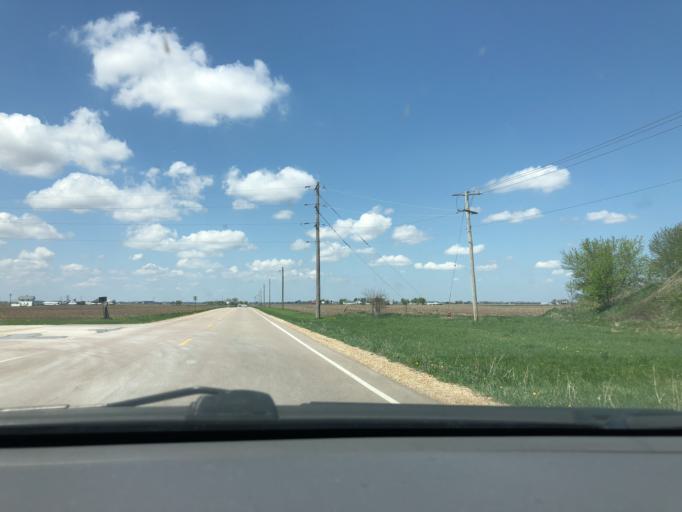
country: US
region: Illinois
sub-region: Kane County
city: Hampshire
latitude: 42.1064
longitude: -88.5436
